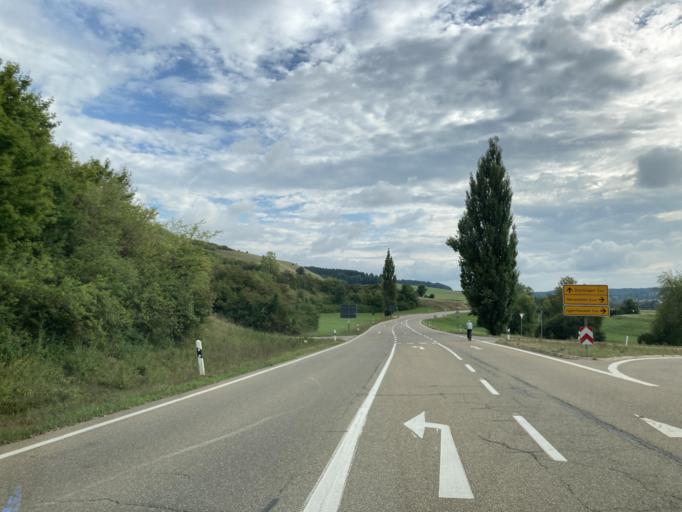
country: DE
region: Baden-Wuerttemberg
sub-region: Regierungsbezirk Stuttgart
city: Dischingen
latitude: 48.7157
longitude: 10.3812
